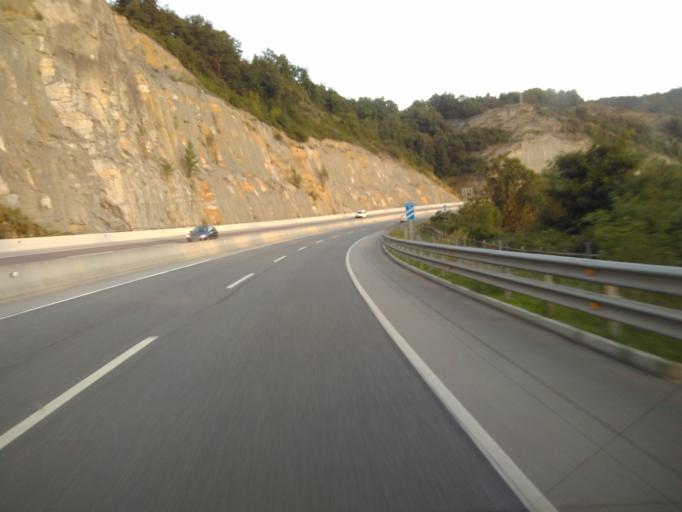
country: ES
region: Catalonia
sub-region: Provincia de Barcelona
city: Vilaseca
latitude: 42.0627
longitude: 2.2379
